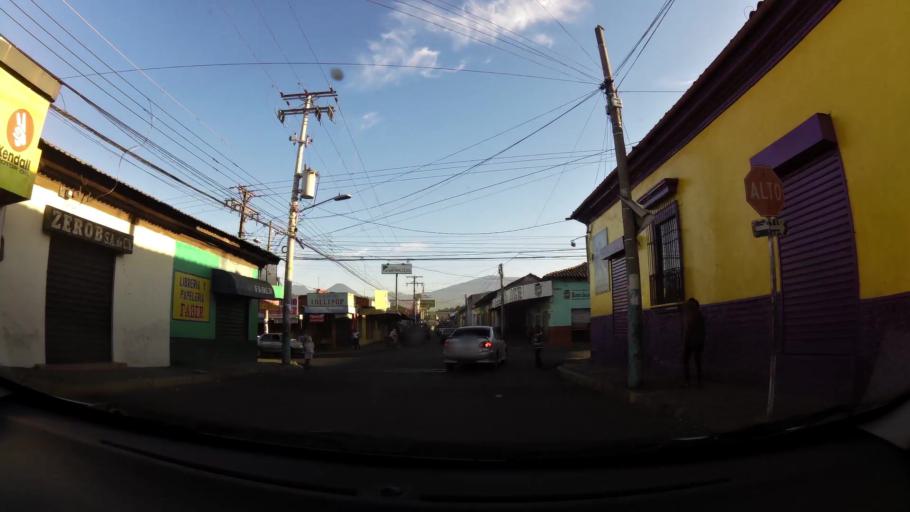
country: SV
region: Sonsonate
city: Sonsonate
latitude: 13.7187
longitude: -89.7257
